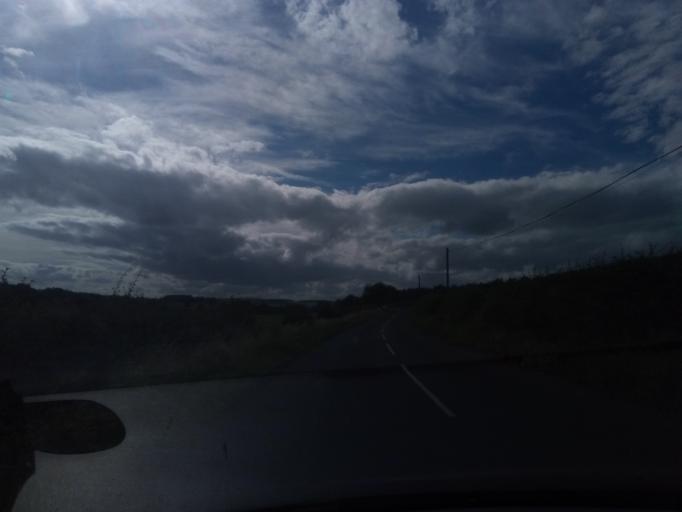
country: GB
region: Scotland
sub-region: The Scottish Borders
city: Coldstream
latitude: 55.5949
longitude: -2.2145
